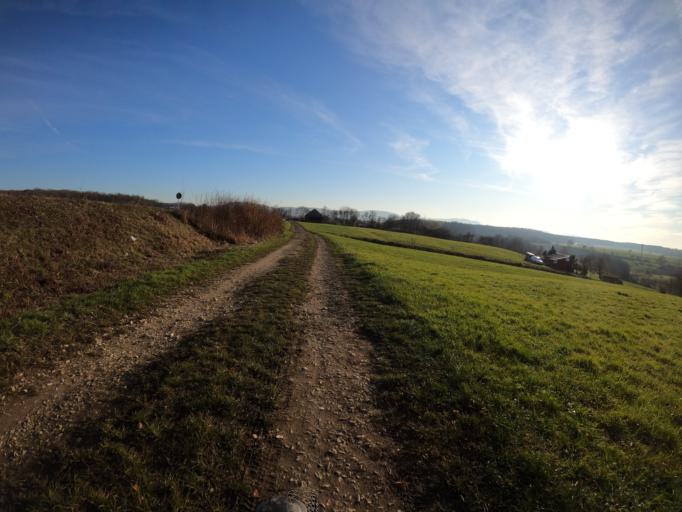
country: DE
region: Baden-Wuerttemberg
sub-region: Regierungsbezirk Stuttgart
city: Wangen
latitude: 48.7010
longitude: 9.6200
